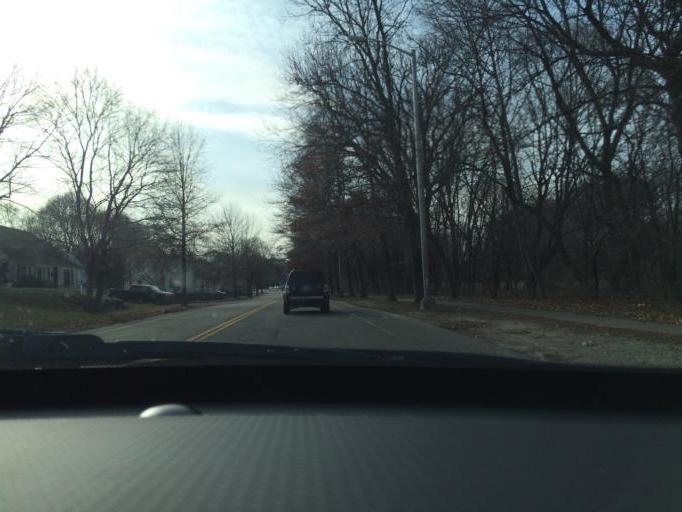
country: US
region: Massachusetts
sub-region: Norfolk County
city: Quincy
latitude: 42.2552
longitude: -71.0227
